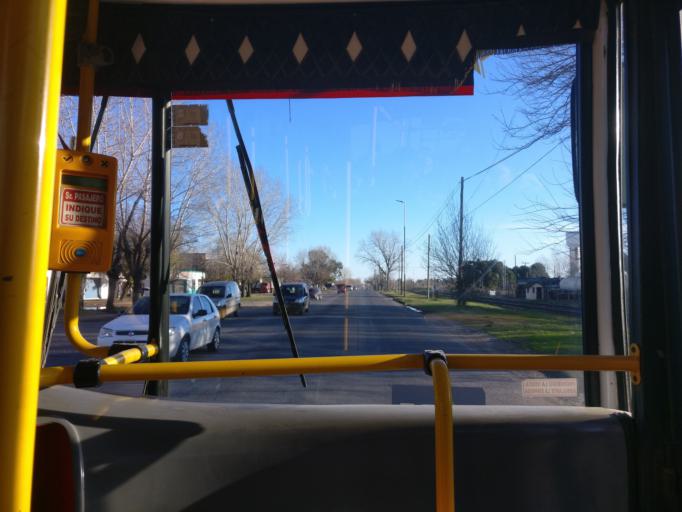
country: AR
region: Buenos Aires
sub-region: Partido de Ezeiza
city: Ezeiza
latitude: -34.9015
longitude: -58.5830
